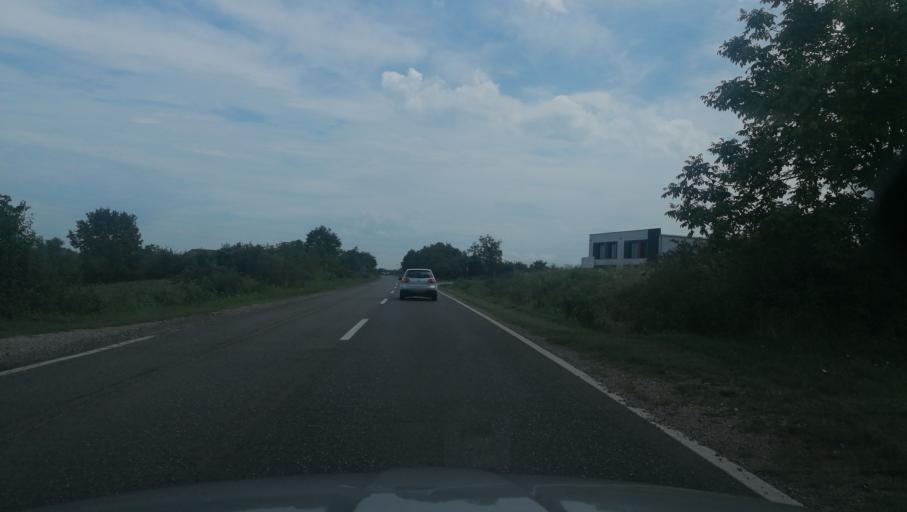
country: BA
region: Federation of Bosnia and Herzegovina
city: Odzak
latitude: 44.9650
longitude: 18.3193
